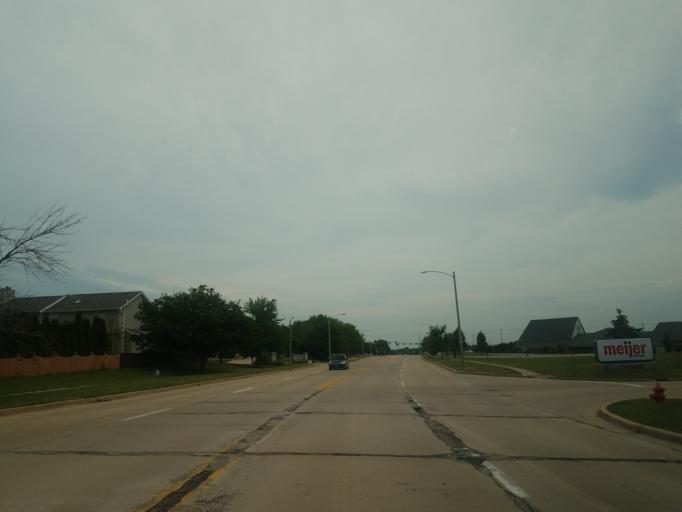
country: US
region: Illinois
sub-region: McLean County
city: Normal
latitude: 40.5131
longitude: -88.9419
